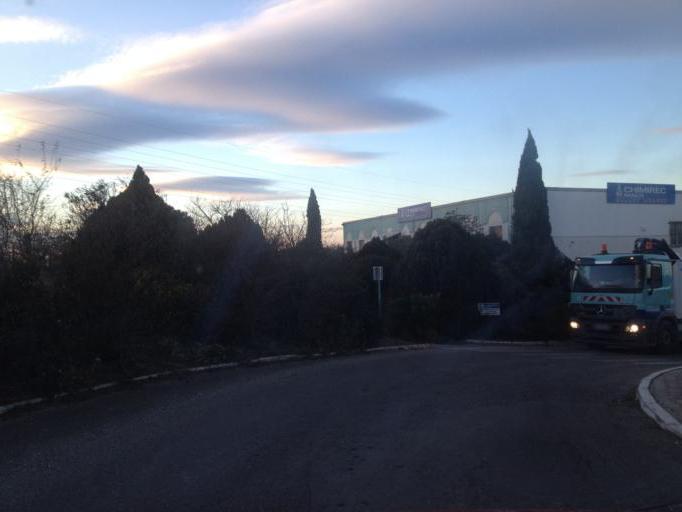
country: FR
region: Provence-Alpes-Cote d'Azur
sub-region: Departement du Vaucluse
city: Orange
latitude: 44.1112
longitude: 4.8366
